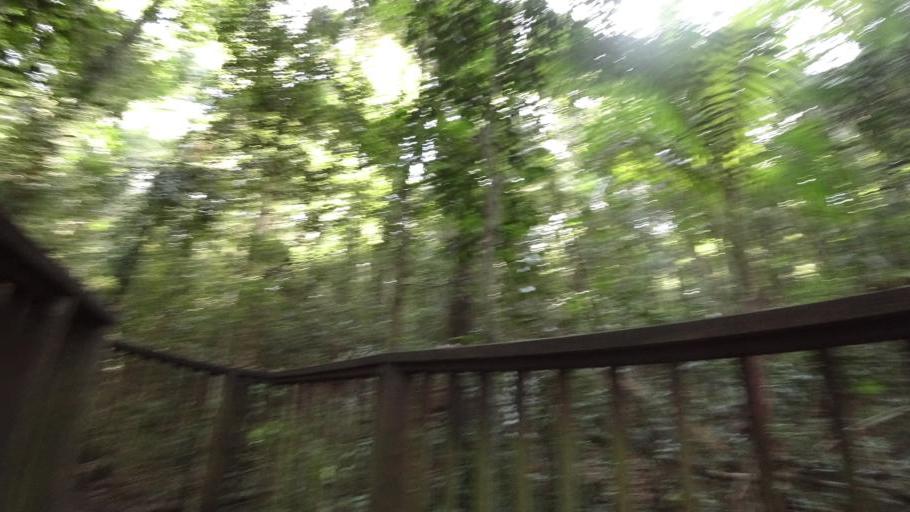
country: AU
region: Queensland
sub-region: Moreton Bay
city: Highvale
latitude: -27.4005
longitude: 152.7914
